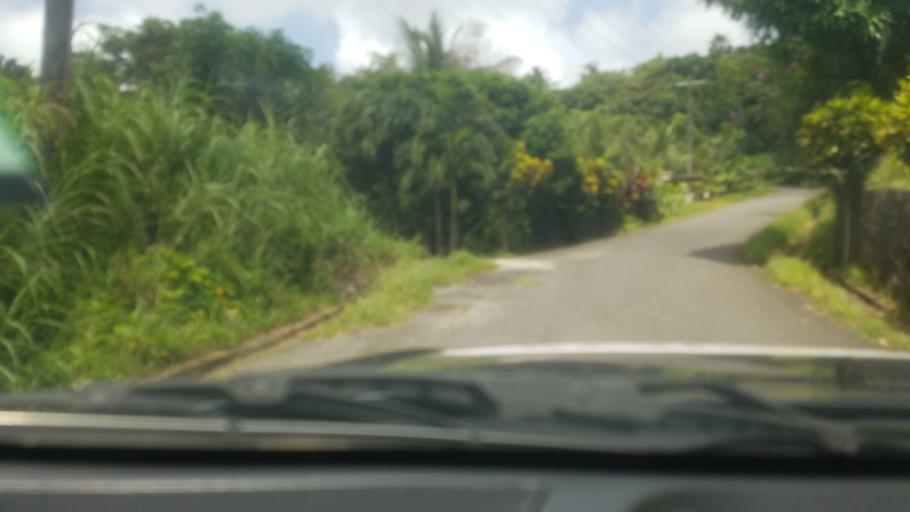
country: LC
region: Laborie Quarter
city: Laborie
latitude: 13.7935
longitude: -60.9537
